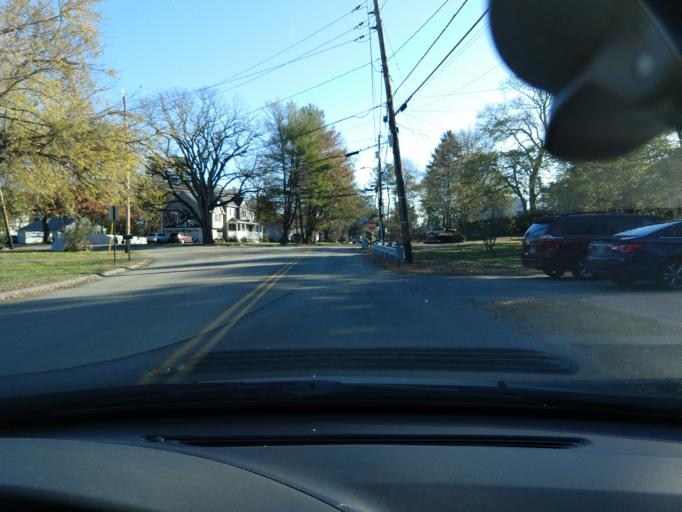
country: US
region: Massachusetts
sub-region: Middlesex County
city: Bedford
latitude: 42.4747
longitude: -71.2701
